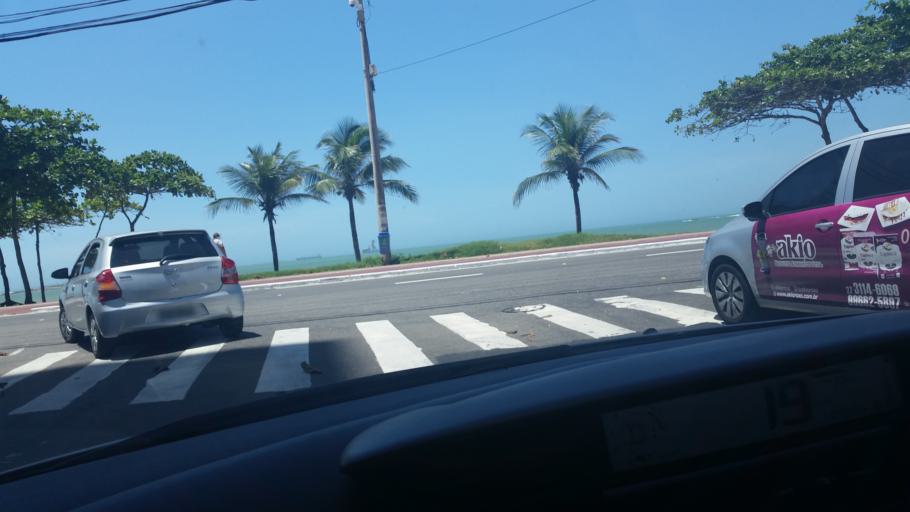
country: BR
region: Espirito Santo
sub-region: Vila Velha
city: Vila Velha
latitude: -20.3581
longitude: -40.2921
